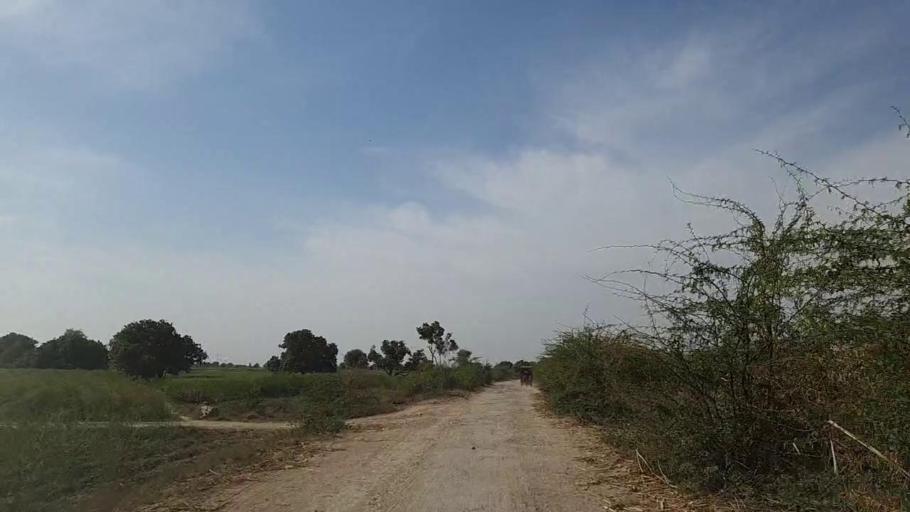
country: PK
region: Sindh
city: Samaro
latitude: 25.2335
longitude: 69.4256
